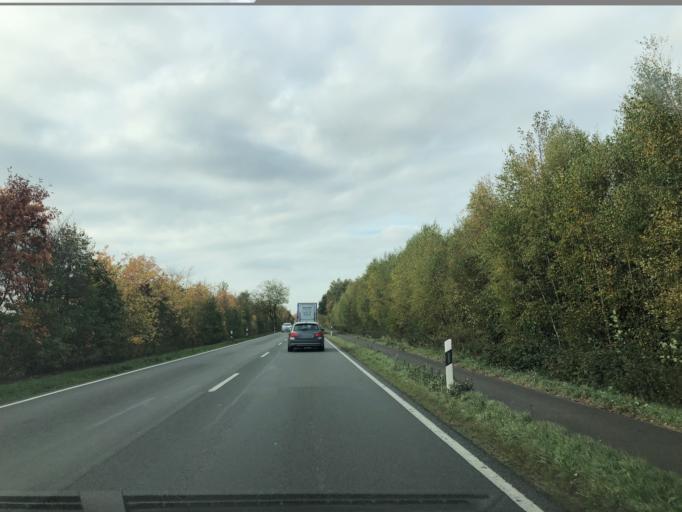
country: DE
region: Lower Saxony
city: Hilkenbrook
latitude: 53.0181
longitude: 7.6762
